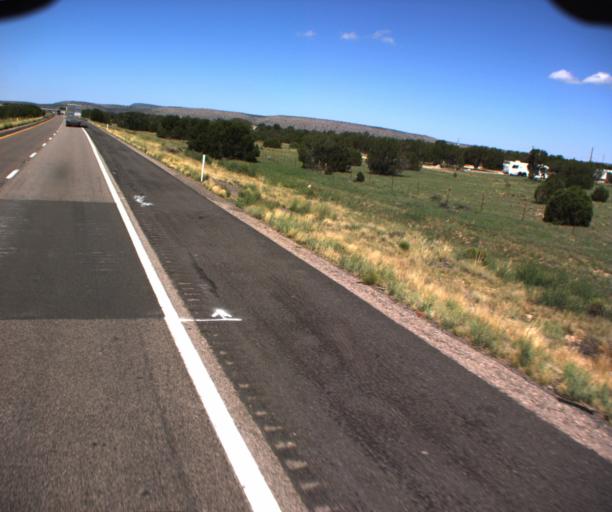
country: US
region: Arizona
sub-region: Mohave County
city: Peach Springs
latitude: 35.3218
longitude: -112.9394
